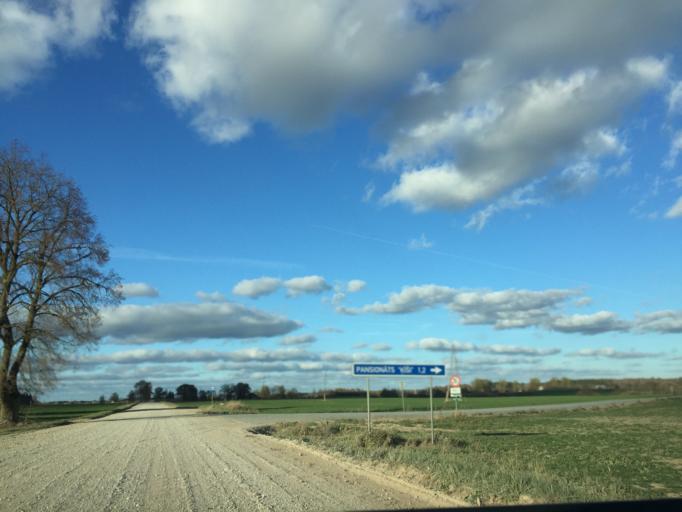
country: LV
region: Tukuma Rajons
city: Tukums
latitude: 56.9343
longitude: 22.9536
